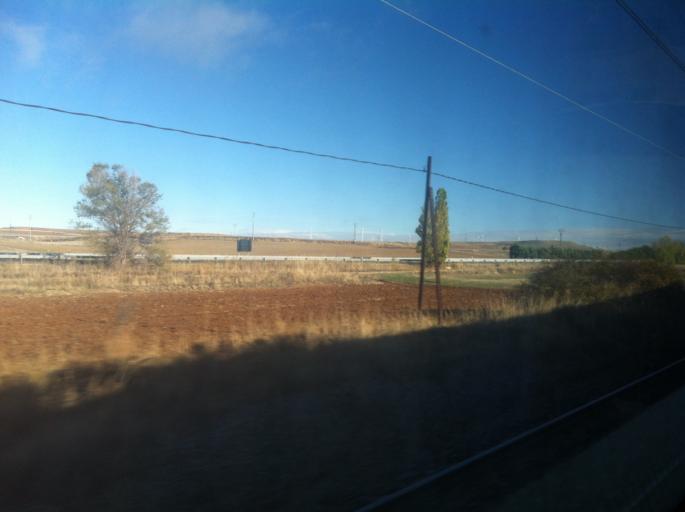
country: ES
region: Castille and Leon
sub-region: Provincia de Burgos
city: Villaverde-Mogina
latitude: 42.1766
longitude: -4.0544
